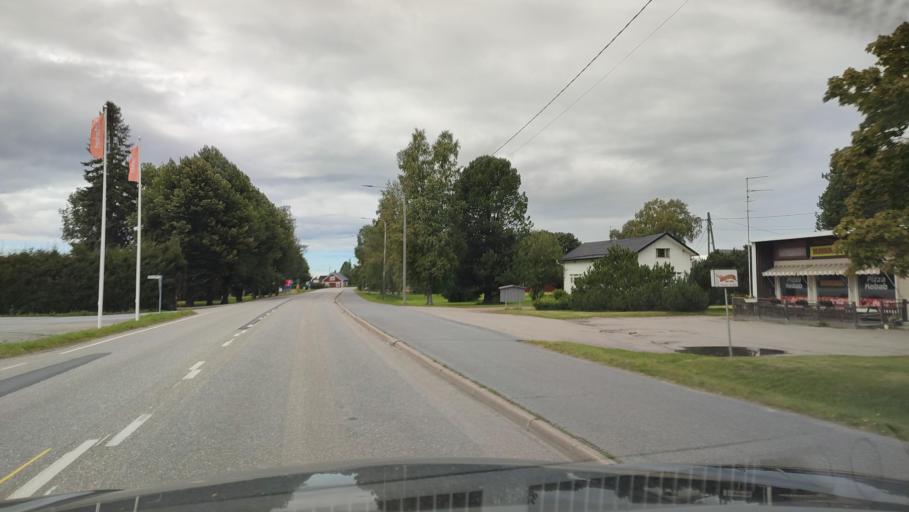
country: FI
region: Ostrobothnia
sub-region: Sydosterbotten
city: Kristinestad
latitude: 62.2548
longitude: 21.5068
